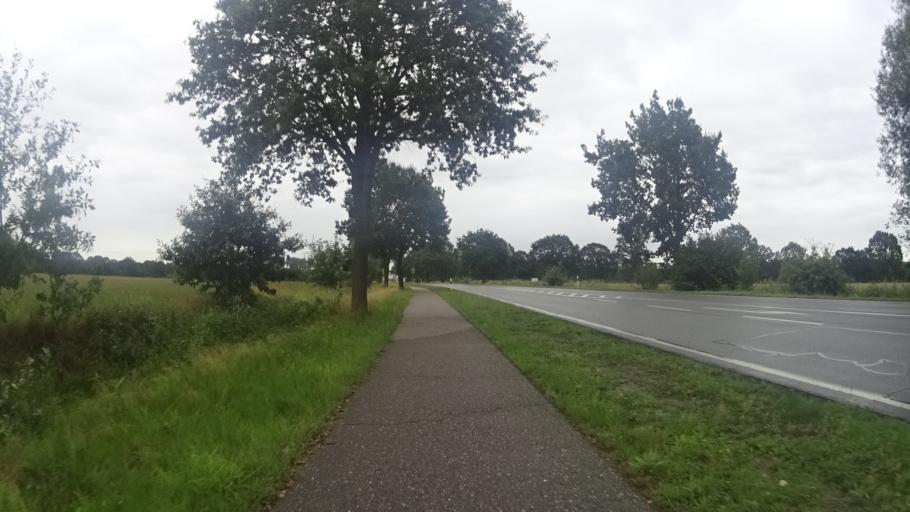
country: DE
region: Schleswig-Holstein
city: Kiebitzreihe
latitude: 53.7811
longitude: 9.6416
